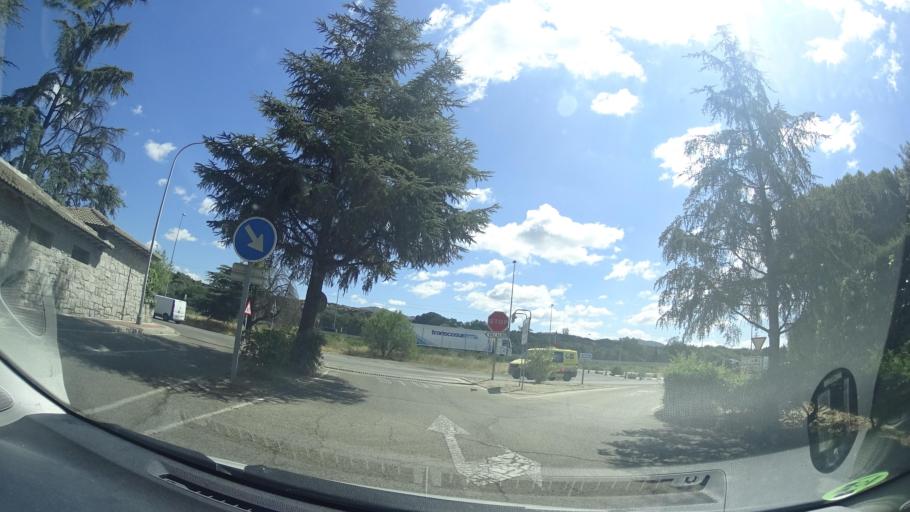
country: ES
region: Madrid
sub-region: Provincia de Madrid
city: Collado-Villalba
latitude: 40.6260
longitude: -3.9941
